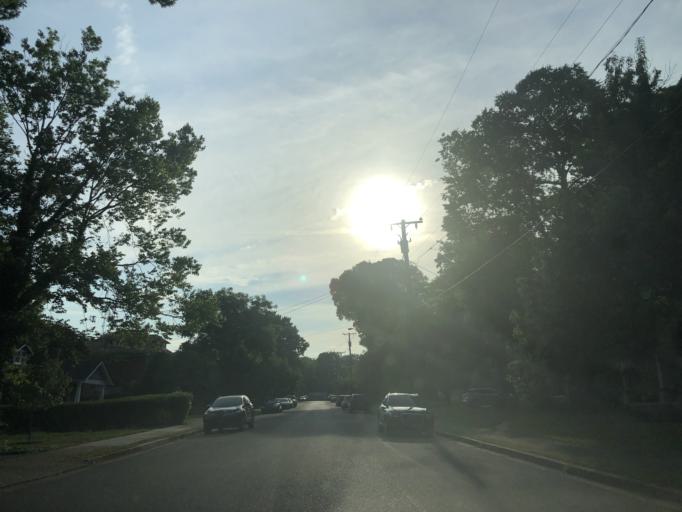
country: US
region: Tennessee
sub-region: Davidson County
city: Nashville
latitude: 36.1318
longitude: -86.7831
